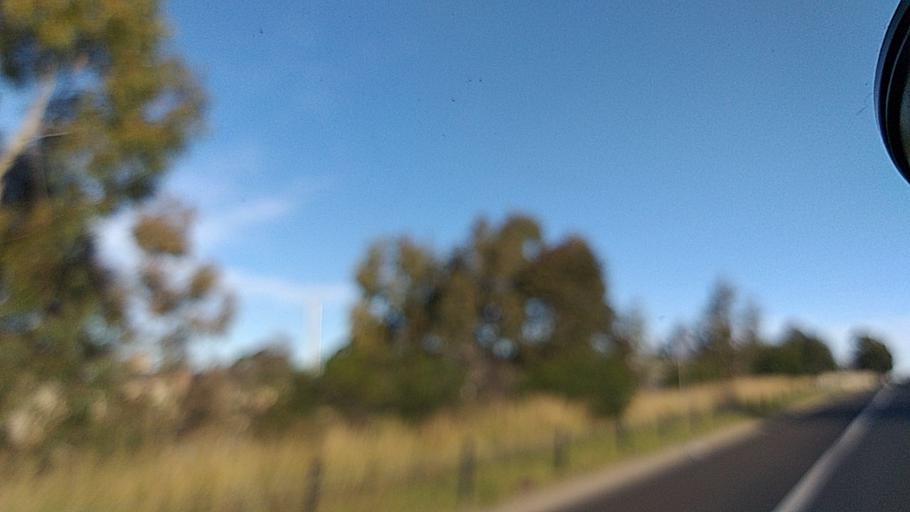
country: AU
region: New South Wales
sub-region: Blacktown
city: Glendenning
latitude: -33.7590
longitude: 150.8476
